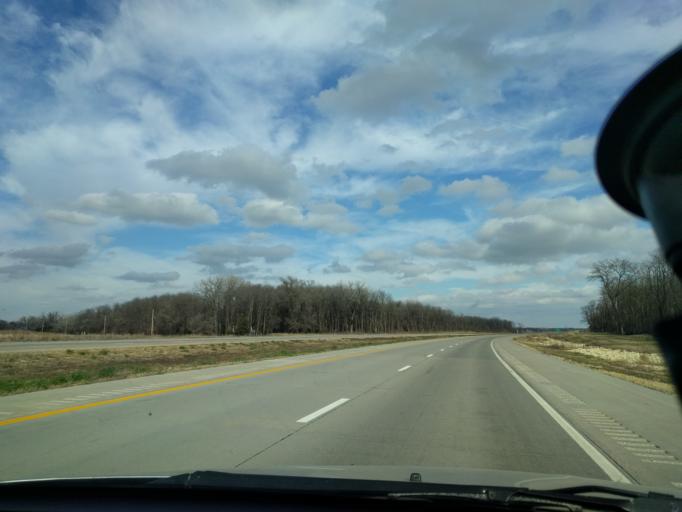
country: US
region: Kansas
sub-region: Reno County
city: Buhler
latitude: 38.1457
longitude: -97.8679
